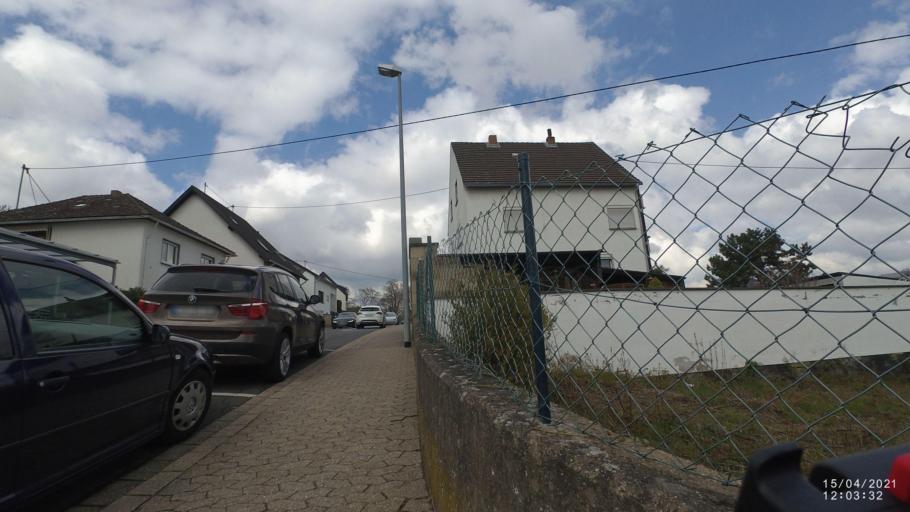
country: DE
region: Rheinland-Pfalz
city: Mendig
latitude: 50.3696
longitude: 7.2776
